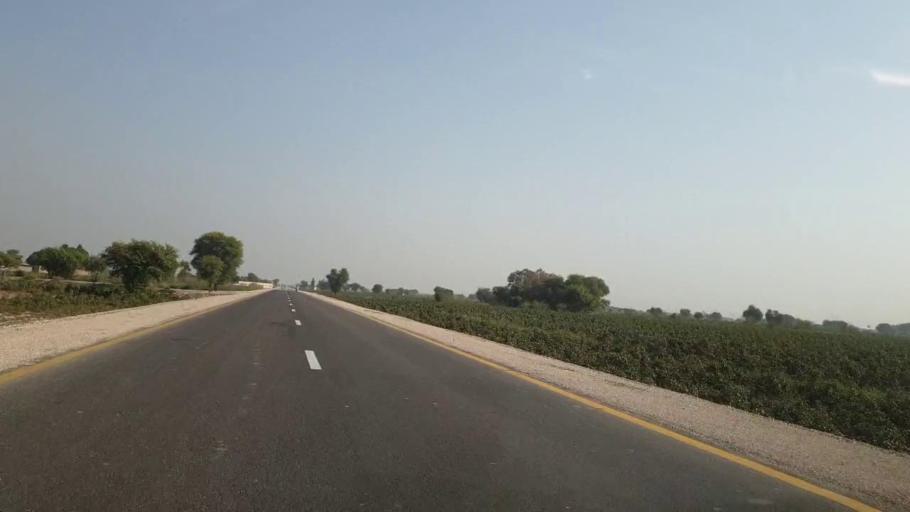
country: PK
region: Sindh
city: Sehwan
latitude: 26.4727
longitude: 67.7902
